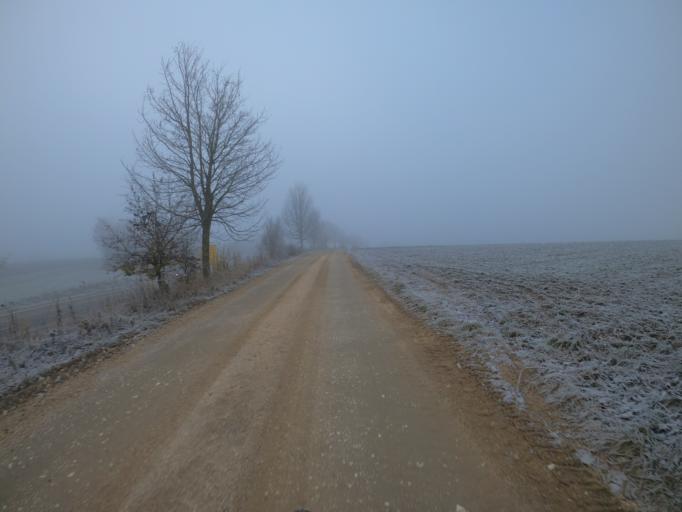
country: DE
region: Baden-Wuerttemberg
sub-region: Tuebingen Region
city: Beimerstetten
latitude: 48.4564
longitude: 9.9813
